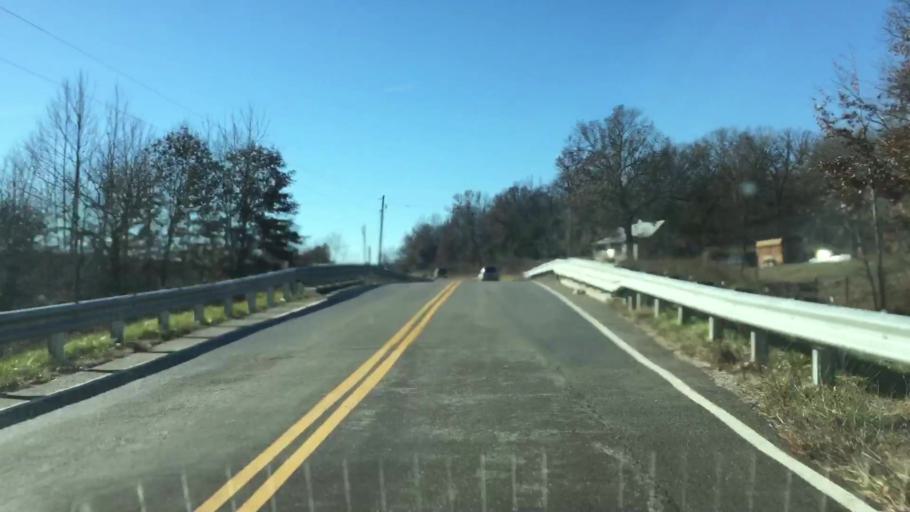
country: US
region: Missouri
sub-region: Miller County
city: Eldon
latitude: 38.3626
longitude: -92.6859
